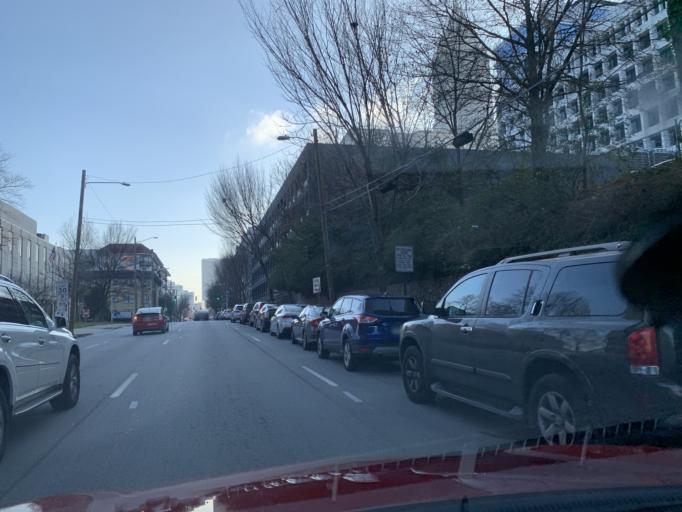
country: US
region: Georgia
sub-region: Fulton County
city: Atlanta
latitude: 33.7747
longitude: -84.3831
